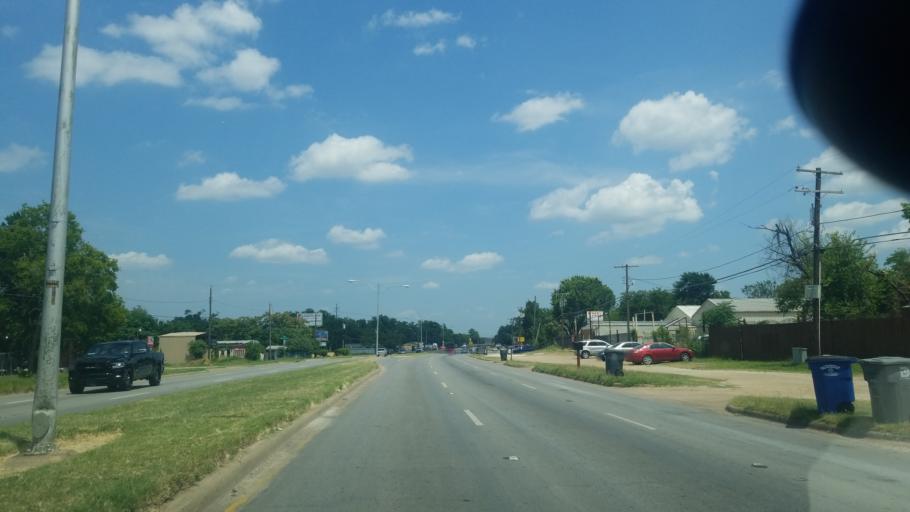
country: US
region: Texas
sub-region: Dallas County
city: Dallas
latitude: 32.7157
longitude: -96.7682
